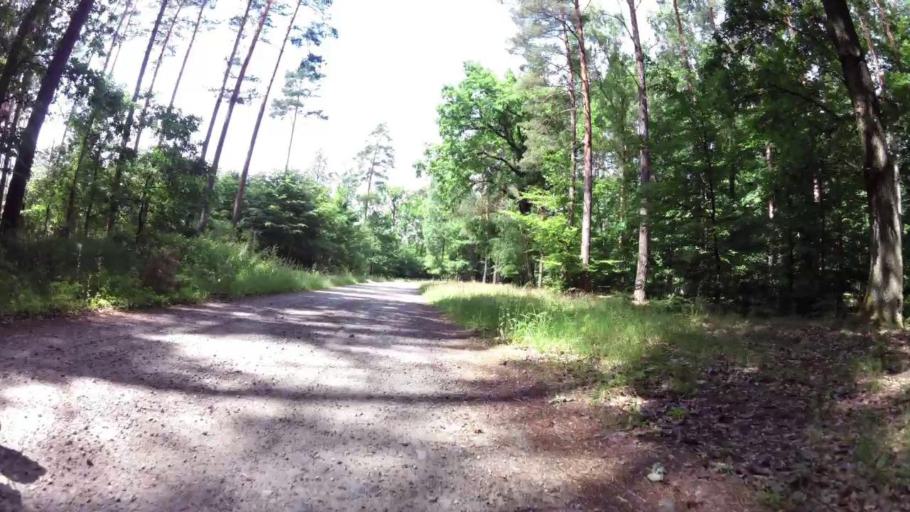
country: PL
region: West Pomeranian Voivodeship
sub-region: Powiat lobeski
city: Lobez
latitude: 53.5690
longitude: 15.6543
